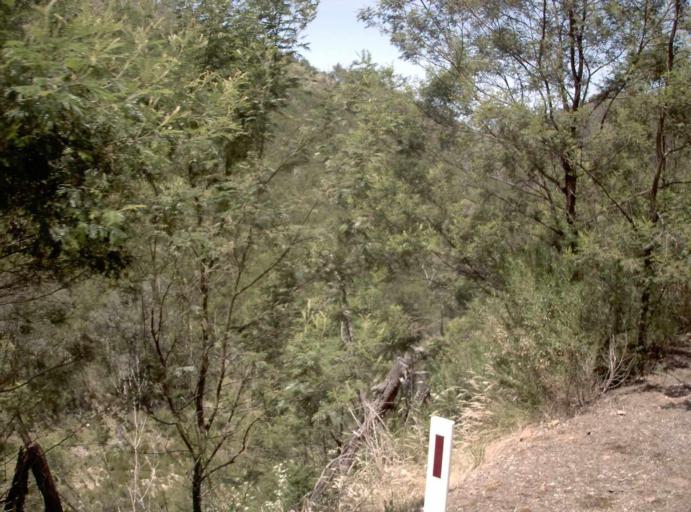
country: AU
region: Victoria
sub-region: East Gippsland
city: Bairnsdale
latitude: -37.4769
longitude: 147.8313
